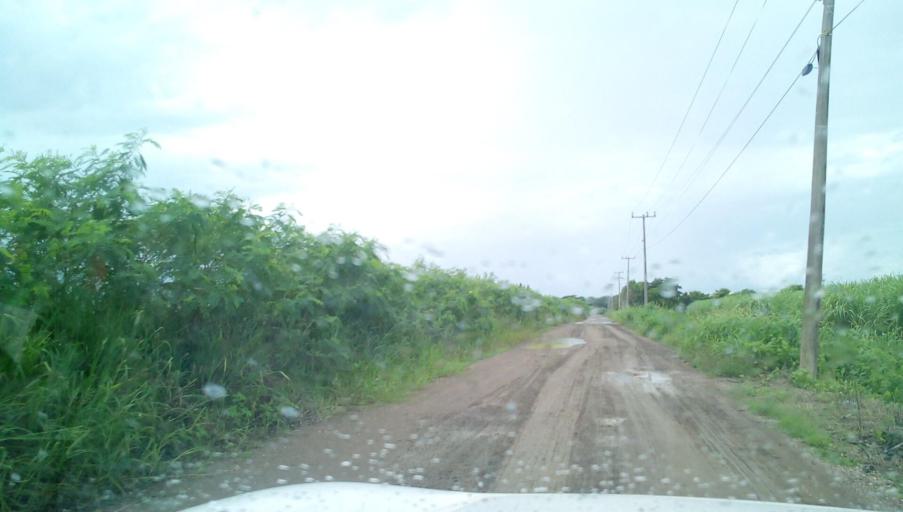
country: MX
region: Veracruz
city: Panuco
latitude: 21.8464
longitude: -98.1175
